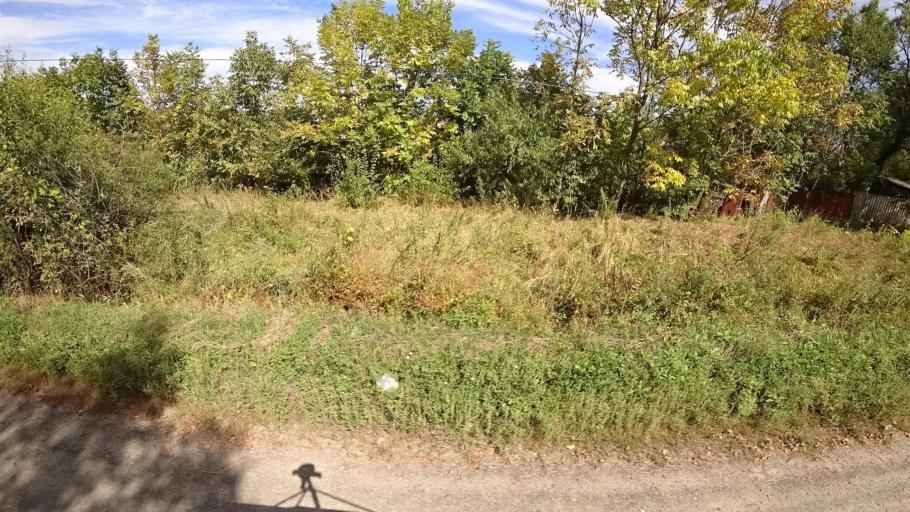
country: RU
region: Primorskiy
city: Yakovlevka
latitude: 44.6407
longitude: 133.5985
